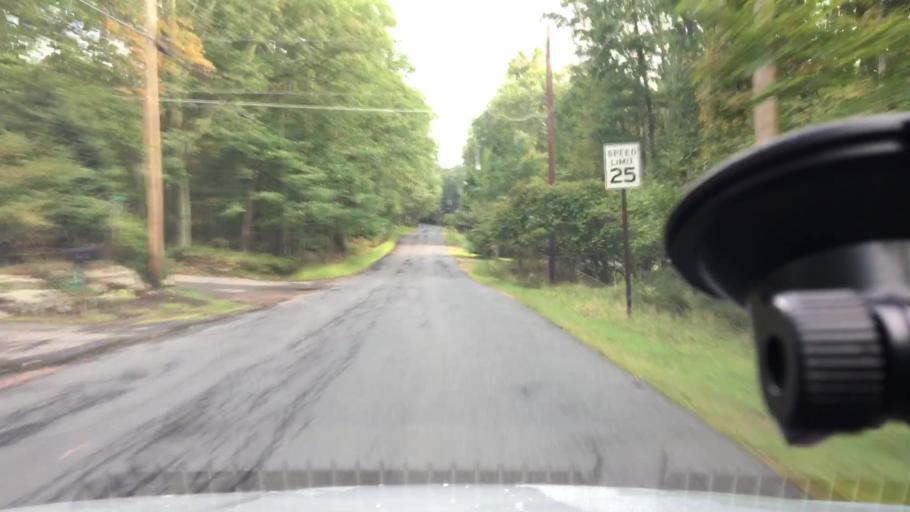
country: US
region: Pennsylvania
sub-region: Monroe County
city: Mountainhome
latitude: 41.1526
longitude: -75.2546
